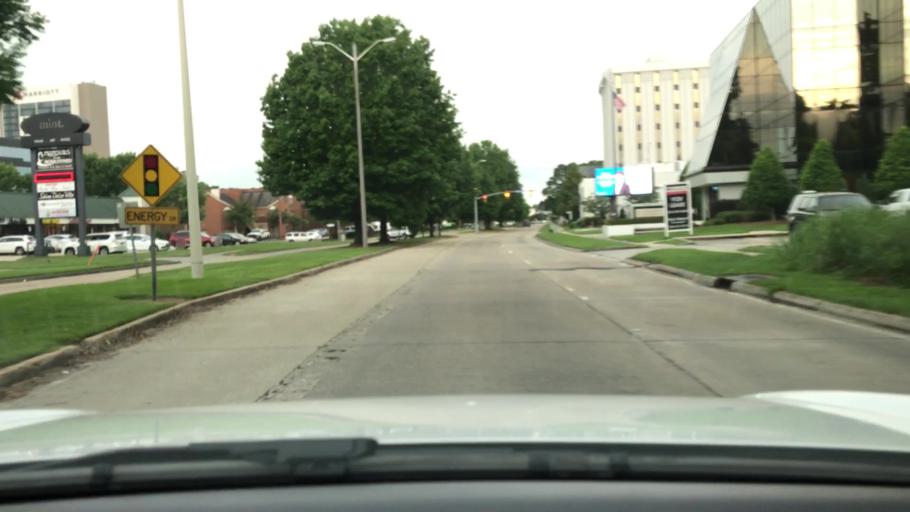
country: US
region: Louisiana
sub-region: East Baton Rouge Parish
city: Baton Rouge
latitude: 30.4251
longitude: -91.1309
